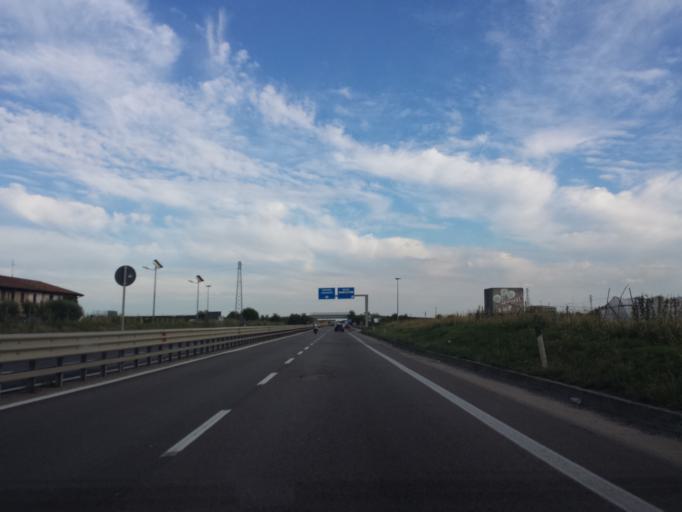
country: IT
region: Veneto
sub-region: Provincia di Verona
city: Campagnola
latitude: 45.3686
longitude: 11.0520
